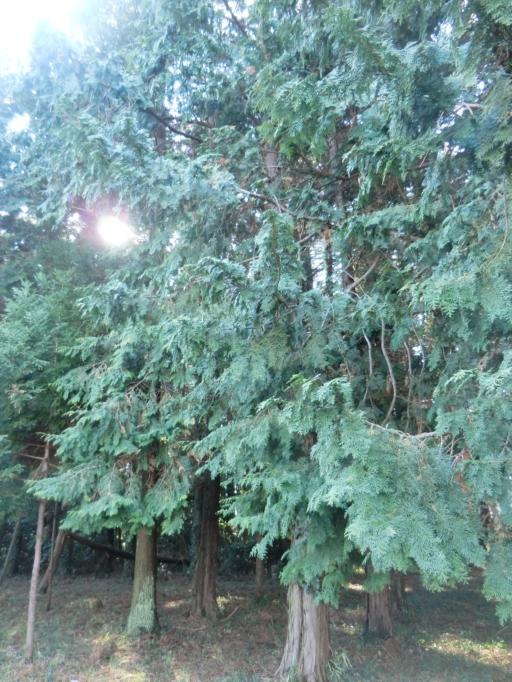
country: JP
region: Ibaraki
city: Naka
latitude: 36.0908
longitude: 140.1203
